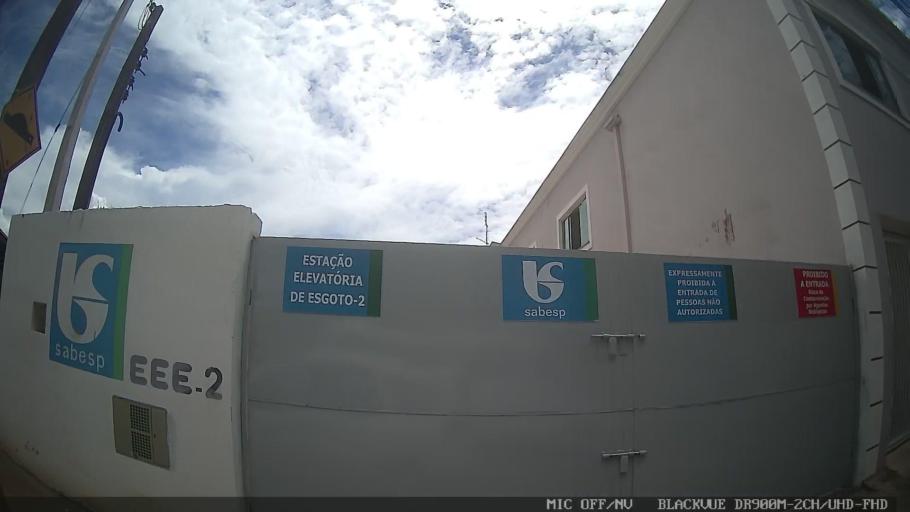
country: BR
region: Sao Paulo
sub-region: Conchas
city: Conchas
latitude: -23.0716
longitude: -47.9775
